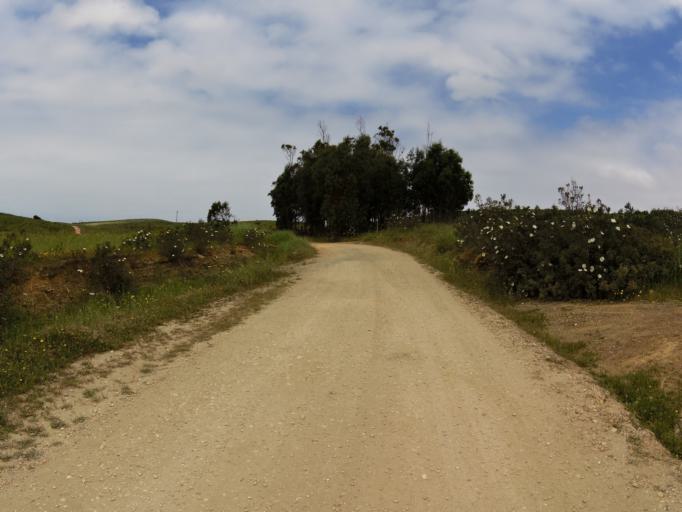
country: PT
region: Faro
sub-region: Vila do Bispo
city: Vila do Bispo
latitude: 37.0866
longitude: -8.8961
